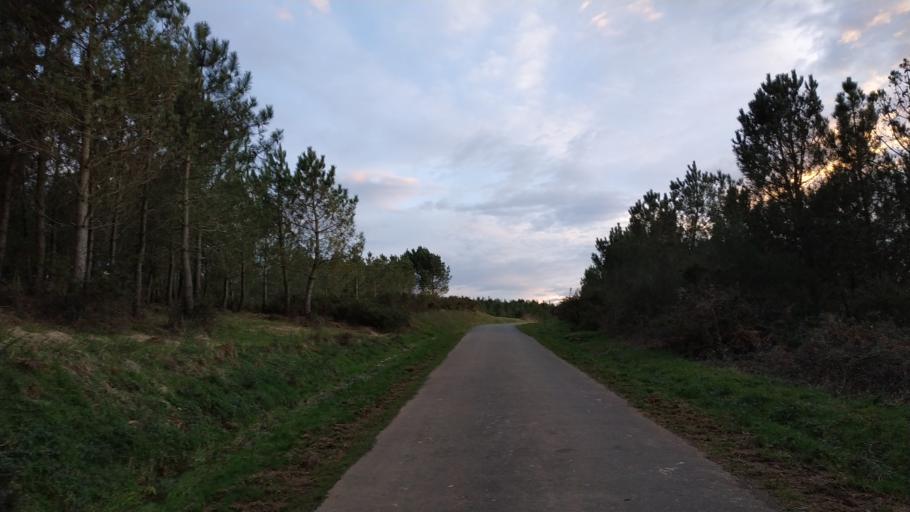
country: ES
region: Galicia
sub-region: Provincia de Pontevedra
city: Silleda
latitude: 42.7671
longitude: -8.1613
